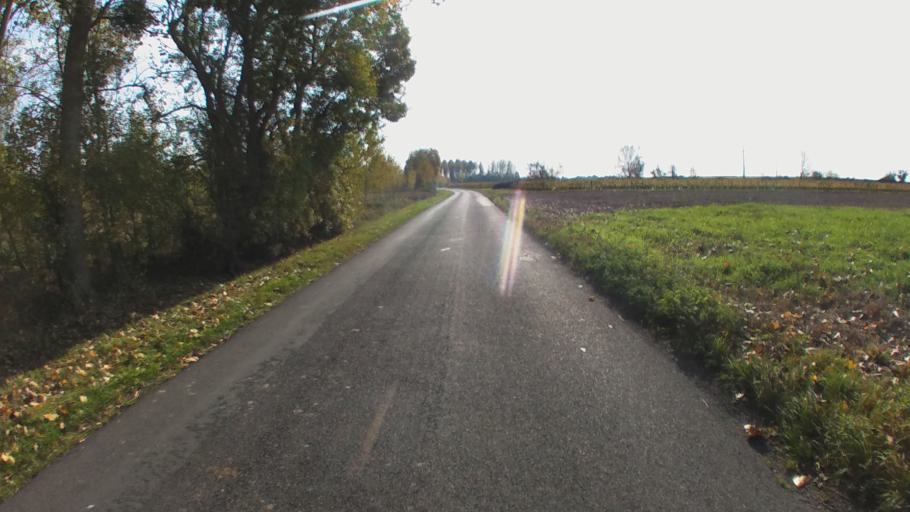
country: FR
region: Pays de la Loire
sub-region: Departement de Maine-et-Loire
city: Chace
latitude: 47.2132
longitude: -0.0904
